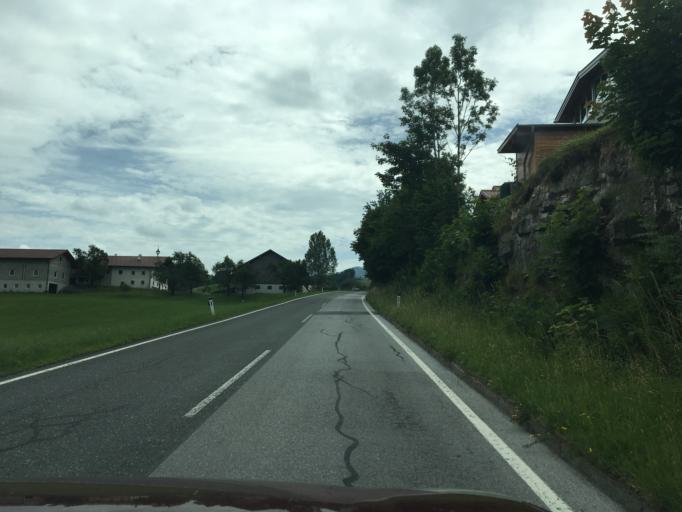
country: AT
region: Salzburg
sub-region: Politischer Bezirk Hallein
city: Kuchl
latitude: 47.6540
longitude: 13.1784
